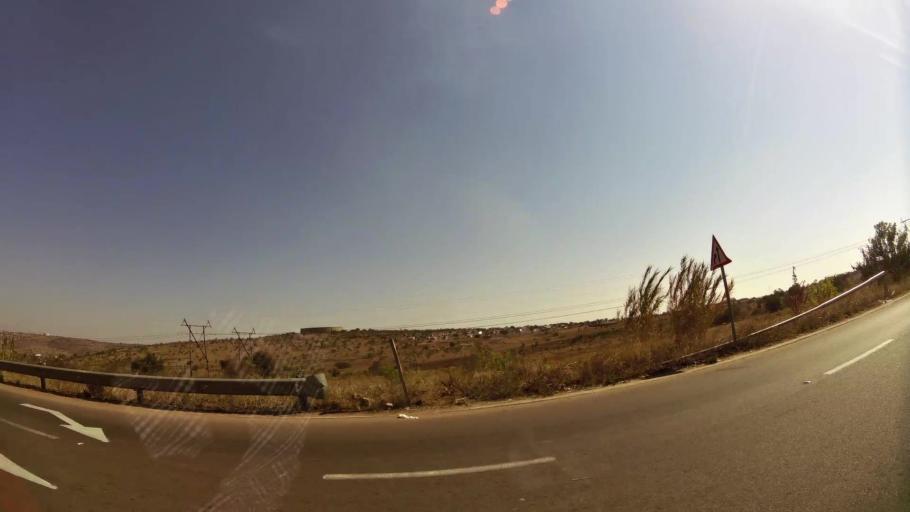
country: ZA
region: Gauteng
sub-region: City of Tshwane Metropolitan Municipality
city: Mabopane
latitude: -25.5285
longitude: 28.0853
